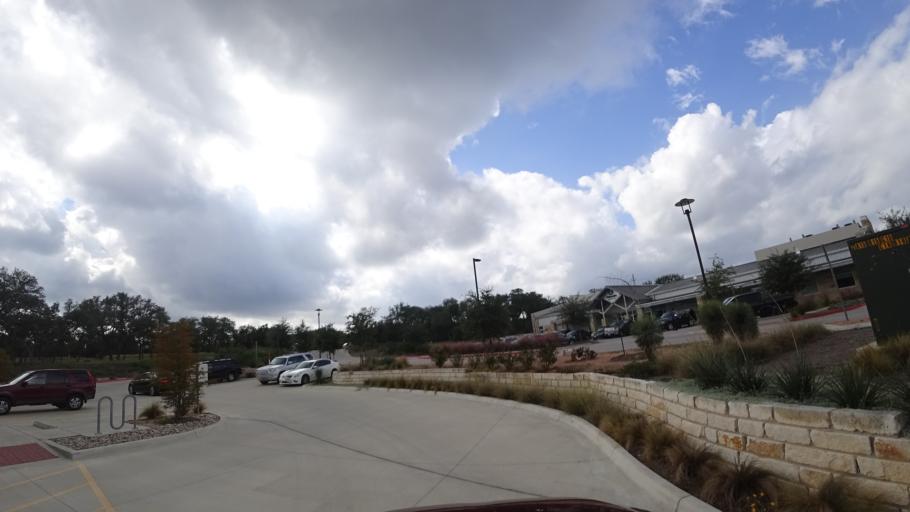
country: US
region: Texas
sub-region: Williamson County
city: Anderson Mill
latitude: 30.4181
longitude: -97.8484
